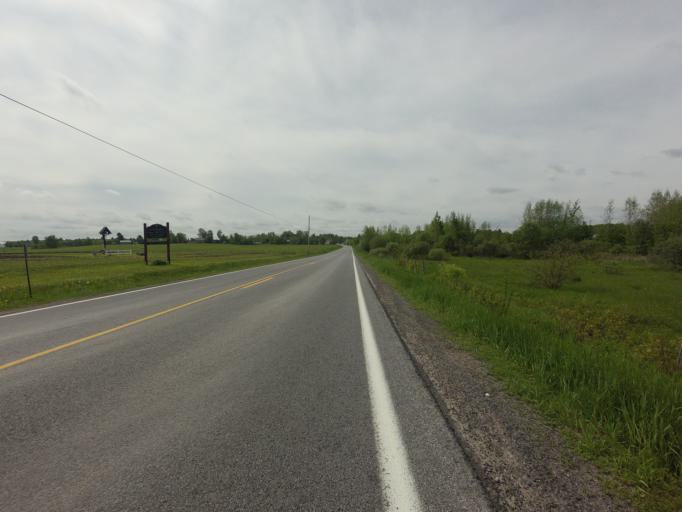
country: CA
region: Ontario
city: Cornwall
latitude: 44.7039
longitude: -74.6592
